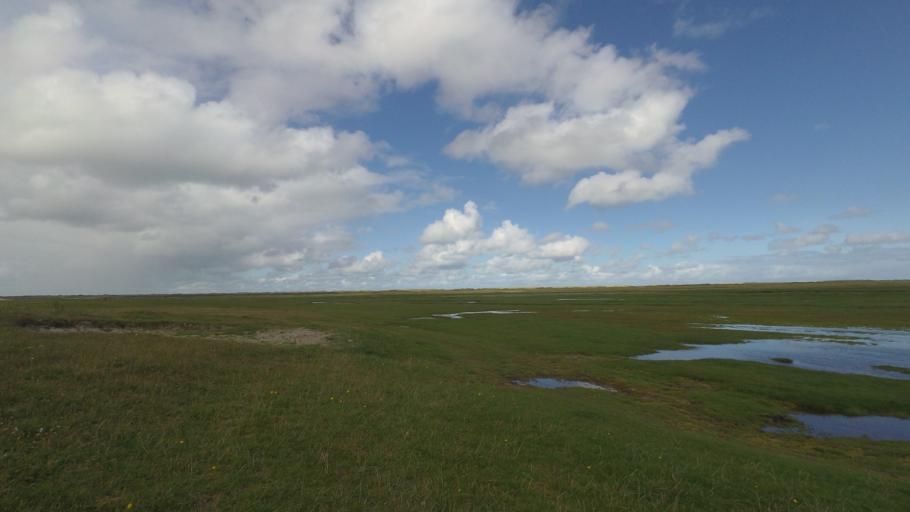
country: NL
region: Friesland
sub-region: Gemeente Ameland
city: Nes
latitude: 53.4490
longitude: 5.8624
